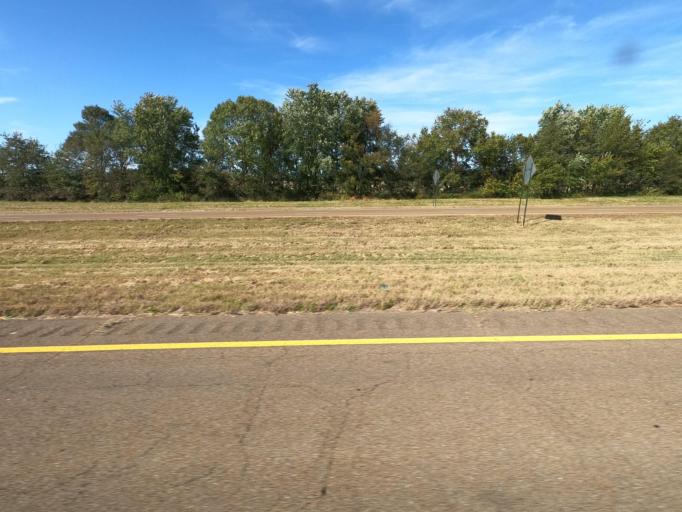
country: US
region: Tennessee
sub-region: Obion County
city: South Fulton
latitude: 36.4701
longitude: -88.9677
